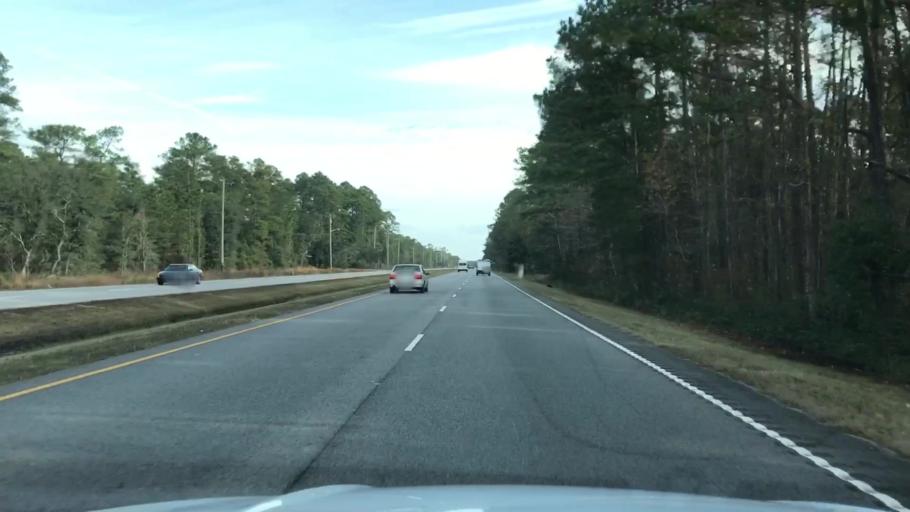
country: US
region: South Carolina
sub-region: Georgetown County
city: Georgetown
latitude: 33.3693
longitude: -79.2193
